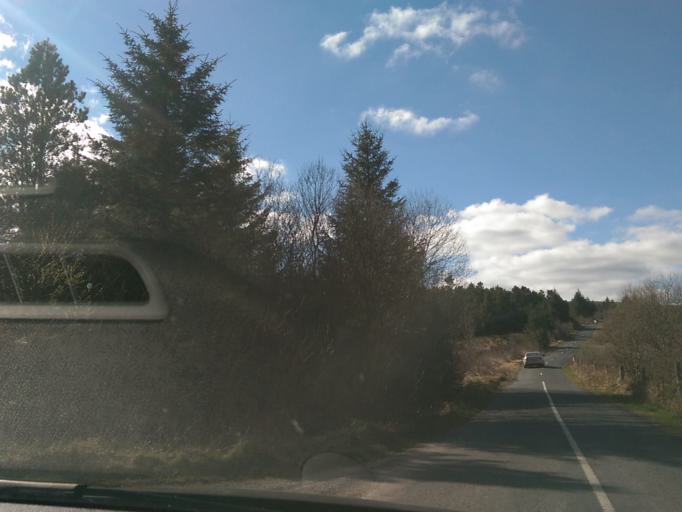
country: IE
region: Leinster
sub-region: Laois
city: Mountrath
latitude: 53.0727
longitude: -7.5814
